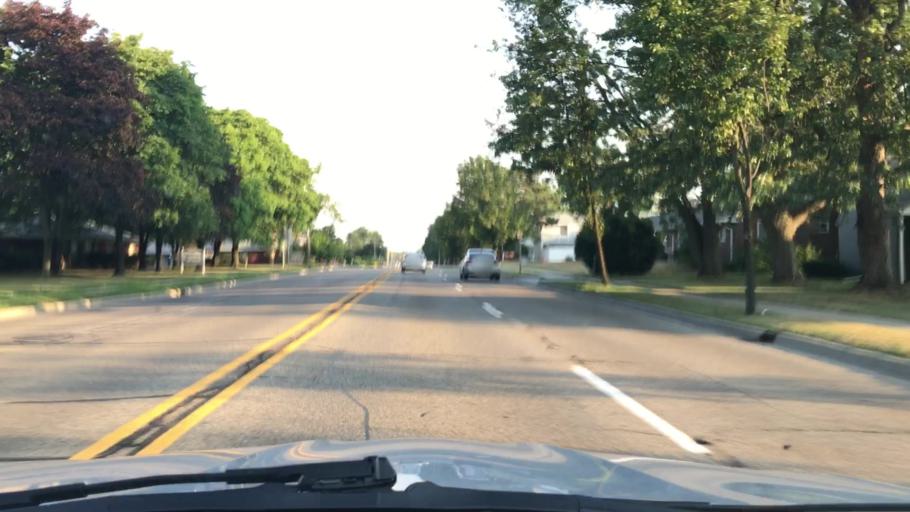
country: US
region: Michigan
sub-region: Oakland County
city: Clawson
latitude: 42.5301
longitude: -83.1654
